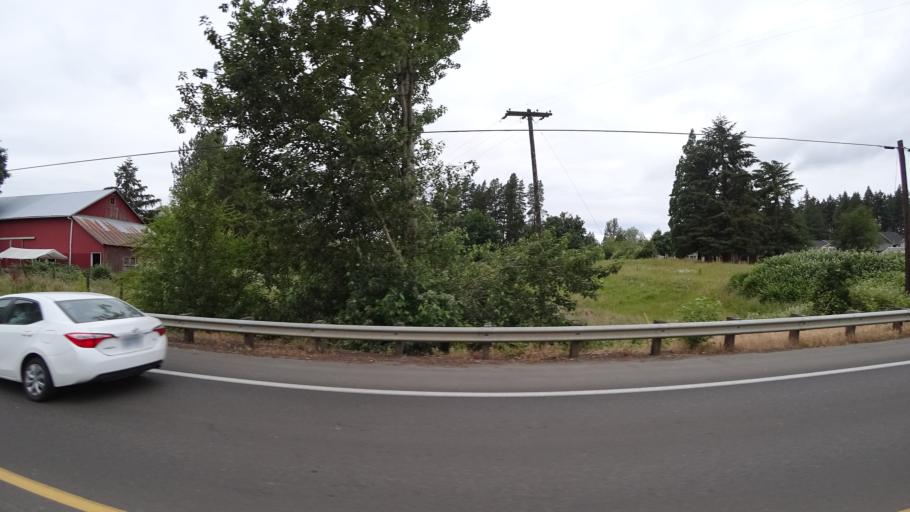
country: US
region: Oregon
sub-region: Washington County
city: Hillsboro
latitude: 45.4895
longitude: -122.9394
